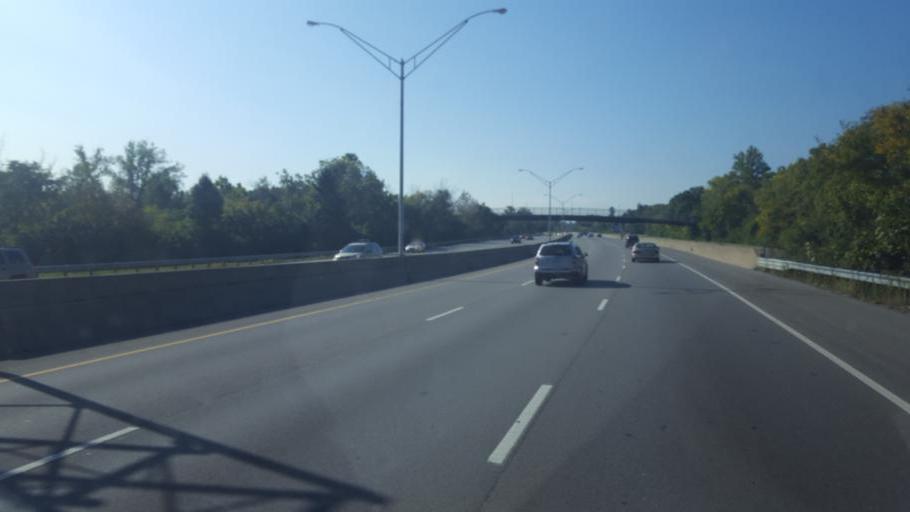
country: US
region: Ohio
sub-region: Franklin County
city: Worthington
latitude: 40.0492
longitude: -83.0336
